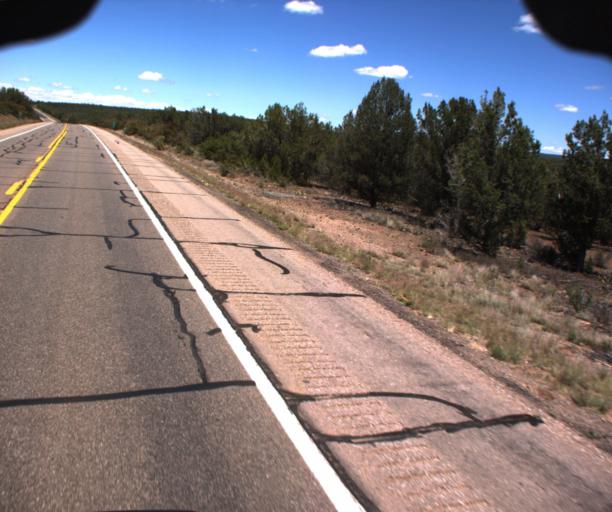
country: US
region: Arizona
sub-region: Yavapai County
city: Paulden
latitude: 35.0489
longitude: -112.3962
